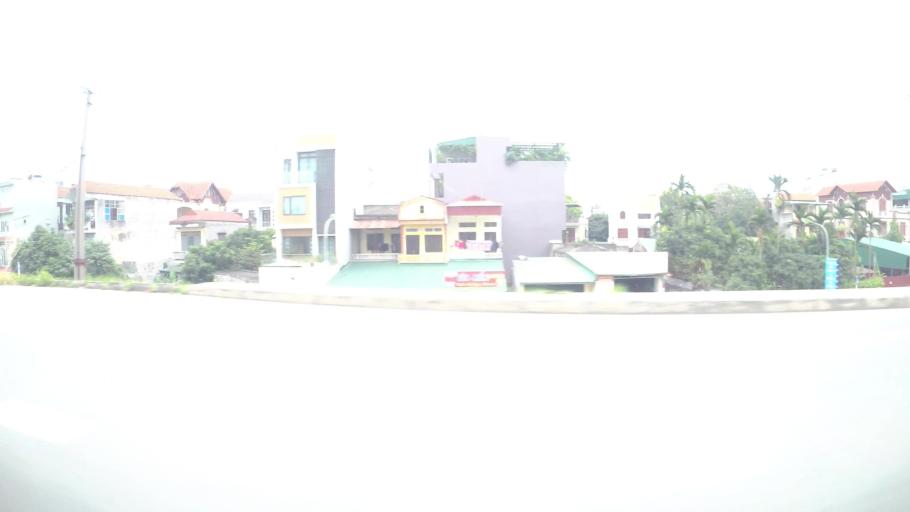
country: VN
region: Ha Noi
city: Hoan Kiem
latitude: 21.0637
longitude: 105.8661
